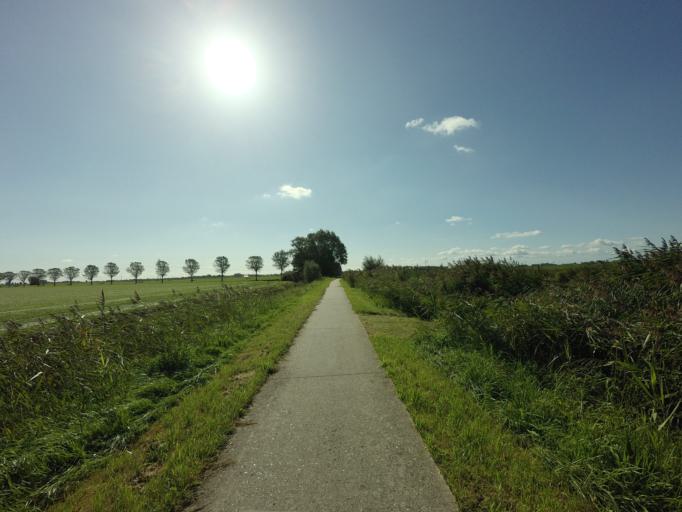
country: NL
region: Friesland
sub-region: Gemeente Boarnsterhim
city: Reduzum
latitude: 53.1215
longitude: 5.7561
